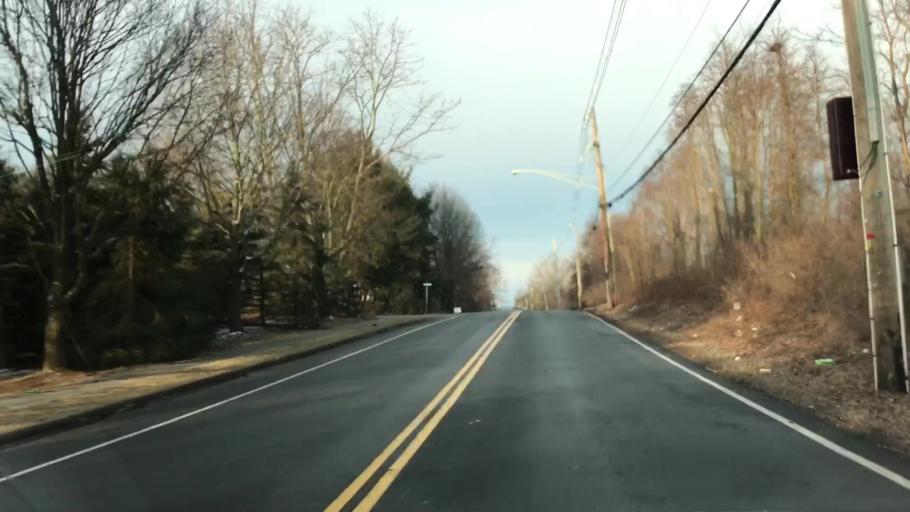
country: US
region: New York
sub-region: Rockland County
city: Viola
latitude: 41.1359
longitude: -74.0719
